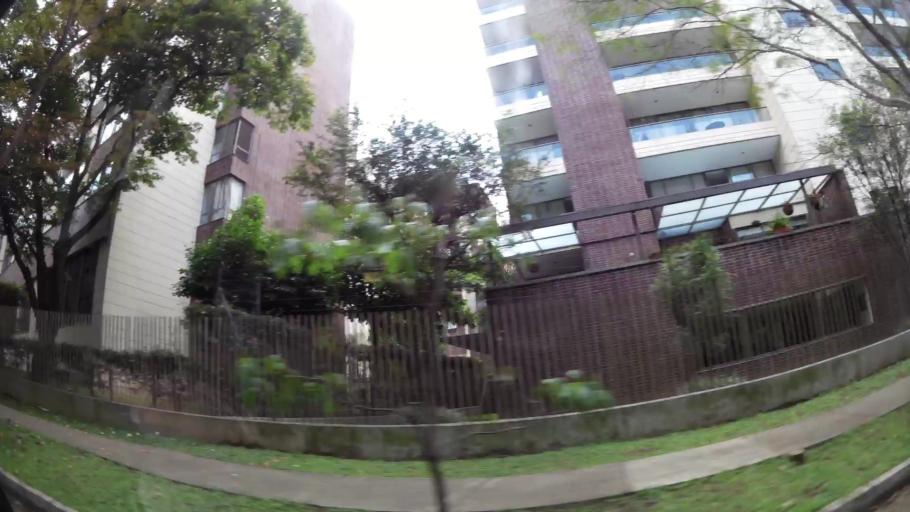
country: CO
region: Antioquia
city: Envigado
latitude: 6.1841
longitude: -75.5813
